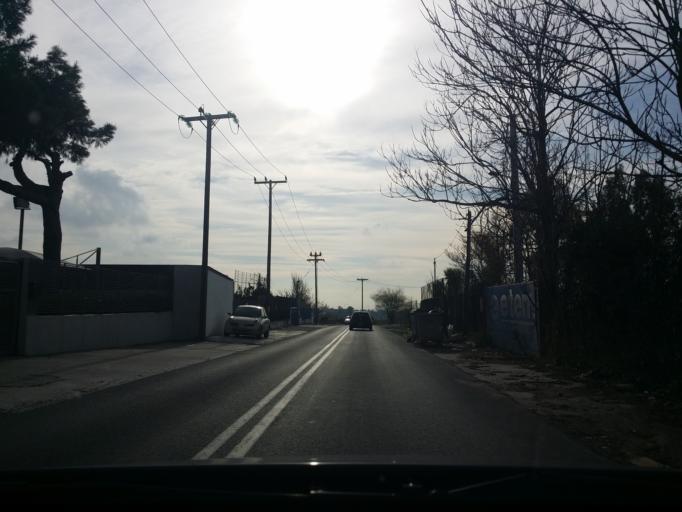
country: GR
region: Attica
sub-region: Nomarchia Athinas
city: Metamorfosi
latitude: 38.0797
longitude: 23.7638
